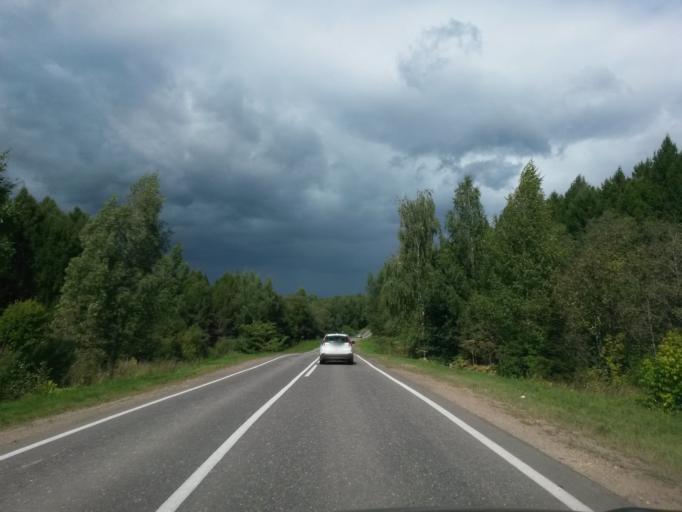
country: RU
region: Jaroslavl
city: Yaroslavl
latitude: 57.7939
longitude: 39.8287
